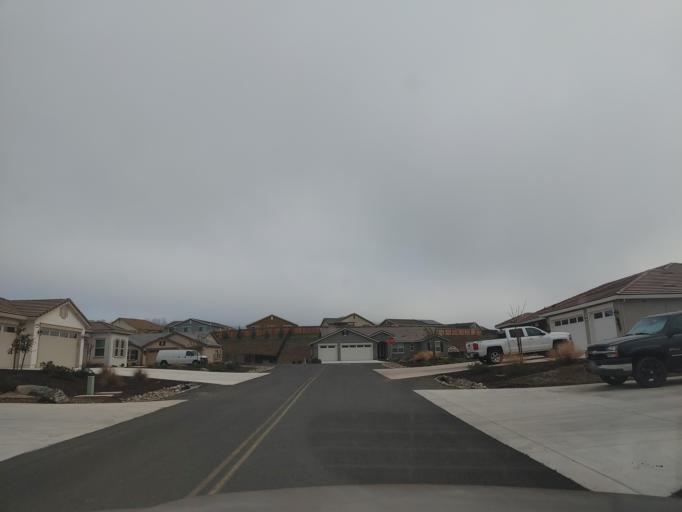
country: US
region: California
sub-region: Calaveras County
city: Copperopolis
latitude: 37.9328
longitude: -120.6092
